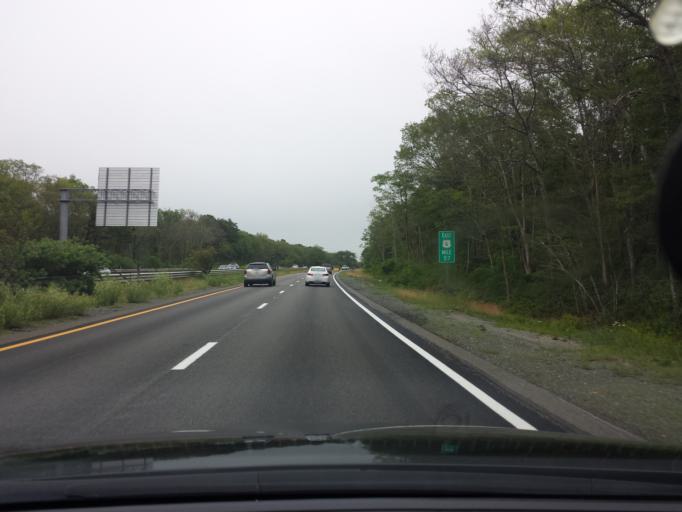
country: US
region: Massachusetts
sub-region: Barnstable County
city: Sagamore
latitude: 41.7554
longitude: -70.5211
